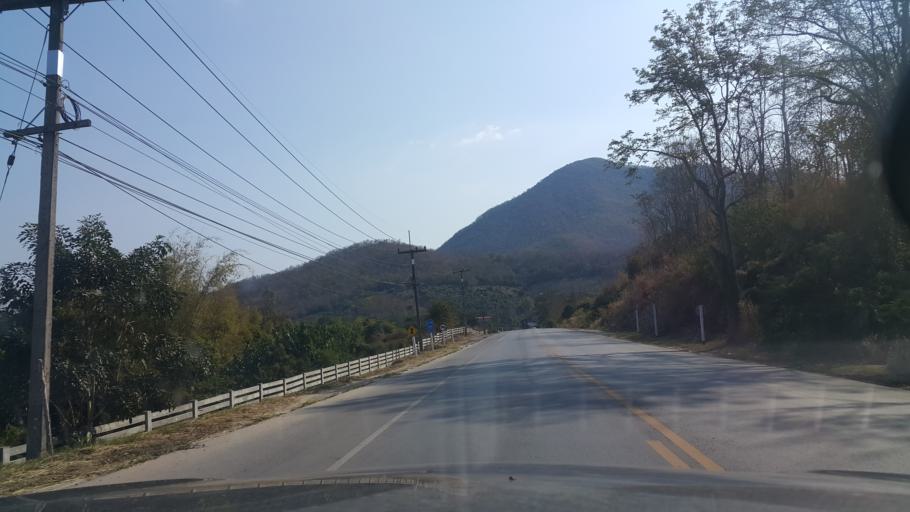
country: LA
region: Vientiane
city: Muang Sanakham
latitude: 17.8981
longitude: 101.7109
